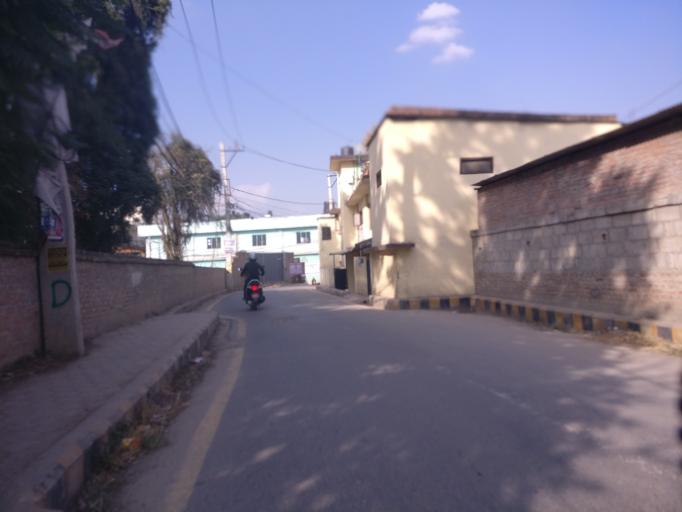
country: NP
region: Central Region
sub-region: Bagmati Zone
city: Patan
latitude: 27.6882
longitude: 85.3141
